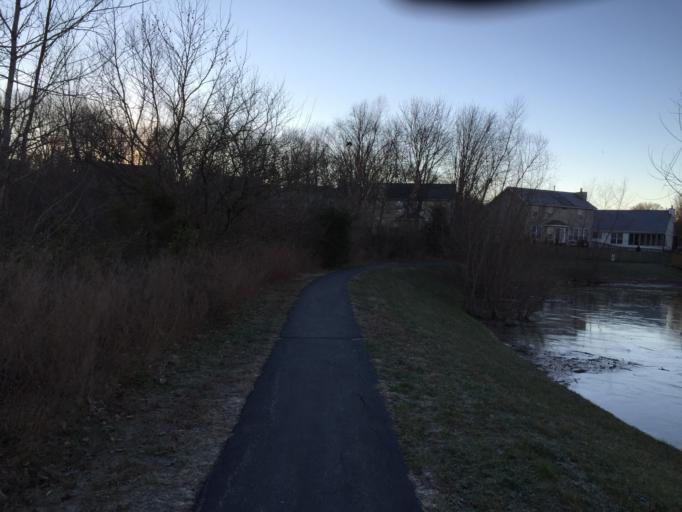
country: US
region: Missouri
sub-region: Saint Louis County
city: Ellisville
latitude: 38.5786
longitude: -90.6105
